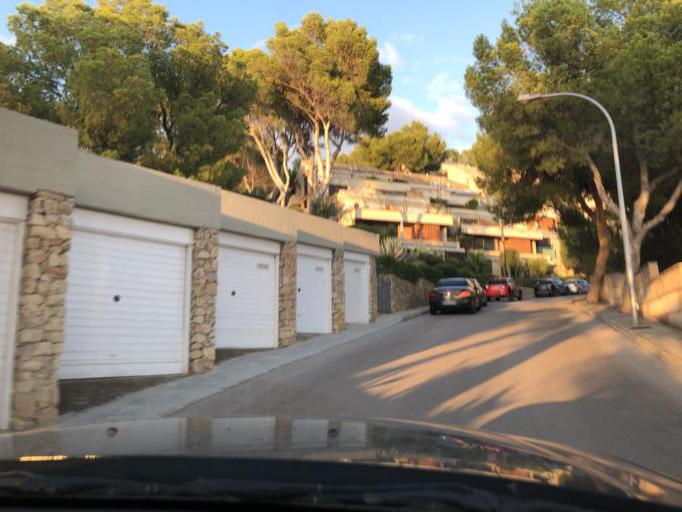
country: ES
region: Balearic Islands
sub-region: Illes Balears
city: Santa Ponsa
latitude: 39.5274
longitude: 2.4631
